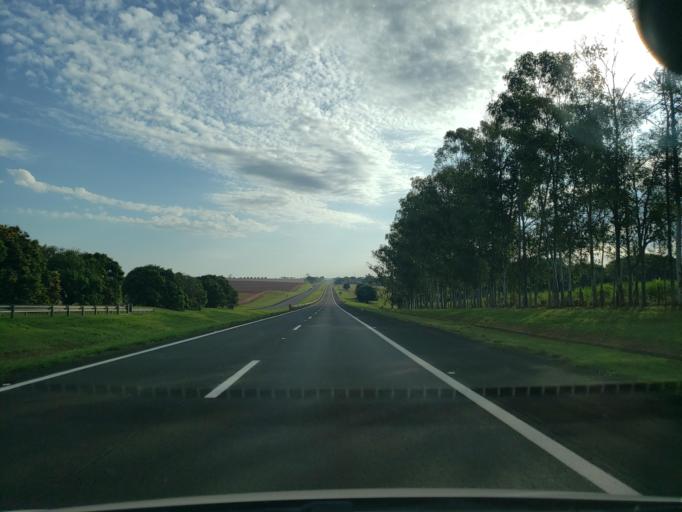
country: BR
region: Sao Paulo
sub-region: Valparaiso
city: Valparaiso
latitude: -21.2064
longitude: -50.7672
